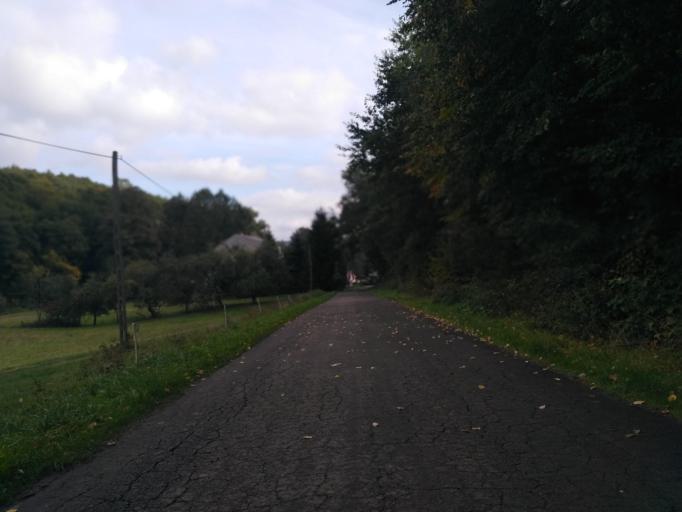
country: PL
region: Subcarpathian Voivodeship
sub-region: Powiat ropczycko-sedziszowski
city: Niedzwiada
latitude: 49.9332
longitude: 21.5355
